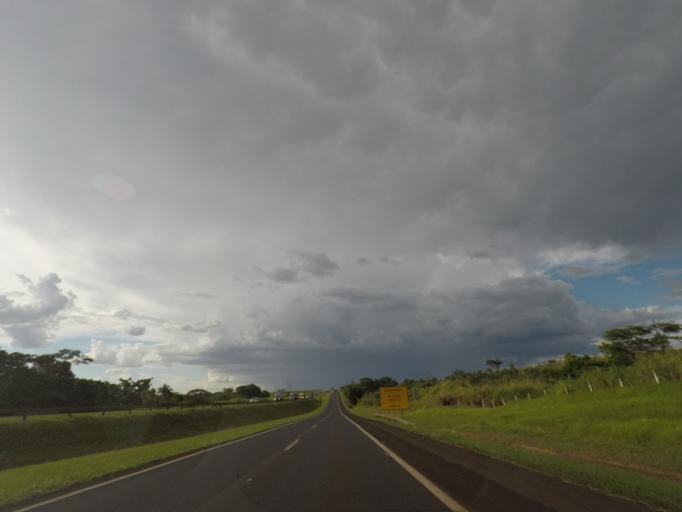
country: BR
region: Sao Paulo
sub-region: Jardinopolis
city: Jardinopolis
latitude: -21.0280
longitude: -47.8364
